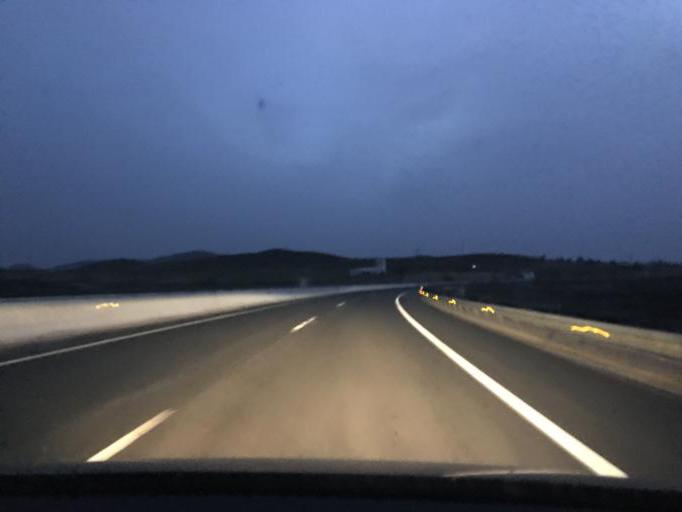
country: ES
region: Andalusia
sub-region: Provincia de Granada
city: Gor
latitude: 37.3936
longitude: -2.9949
